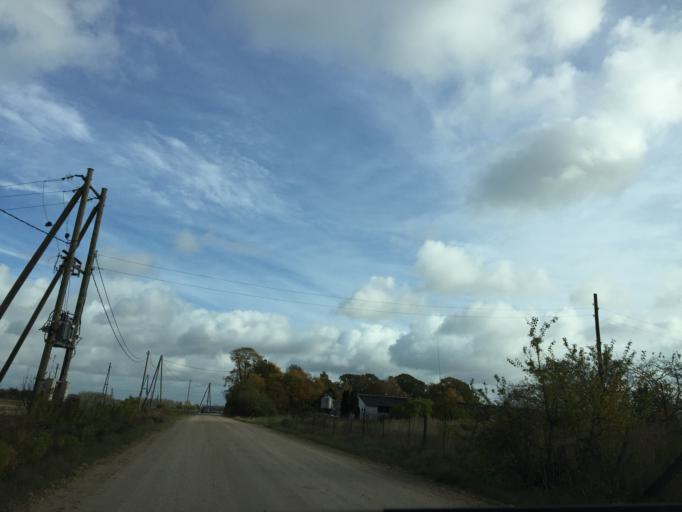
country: LV
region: Lielvarde
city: Lielvarde
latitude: 56.7190
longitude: 24.8429
